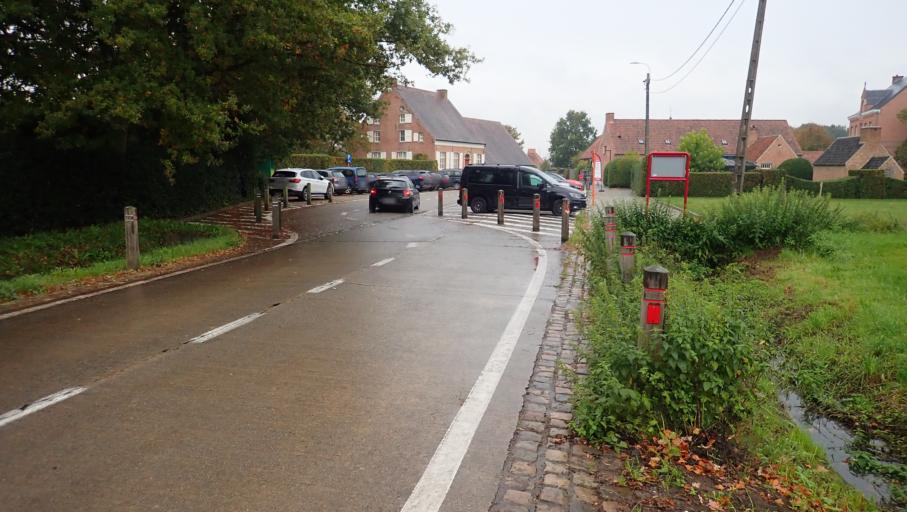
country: BE
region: Flanders
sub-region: Provincie Antwerpen
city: Berlaar
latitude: 51.1269
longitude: 4.6758
